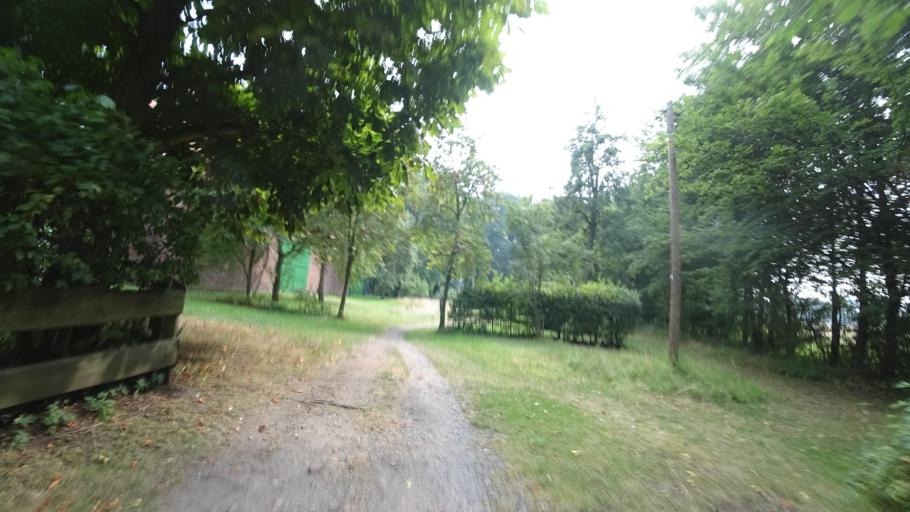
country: DE
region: North Rhine-Westphalia
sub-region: Regierungsbezirk Detmold
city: Guetersloh
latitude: 51.9190
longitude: 8.4379
